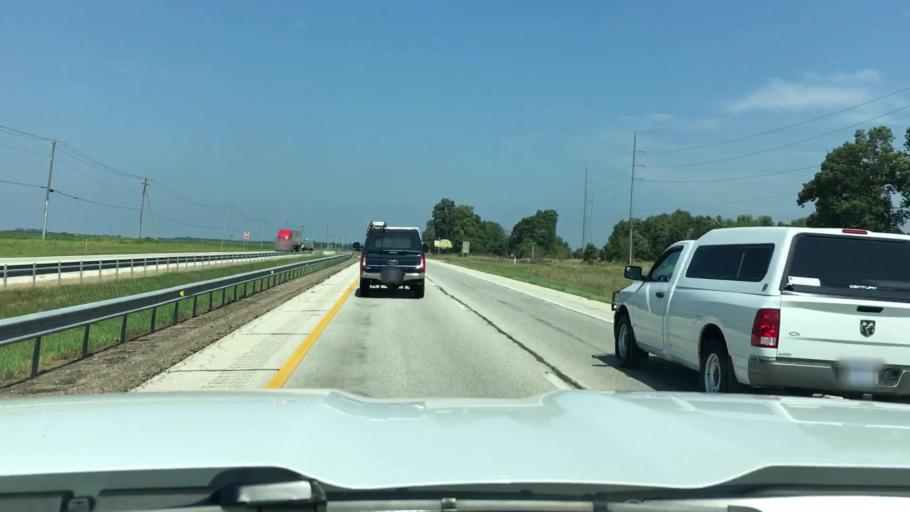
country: US
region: Michigan
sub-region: Kalamazoo County
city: Schoolcraft
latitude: 42.0664
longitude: -85.6362
